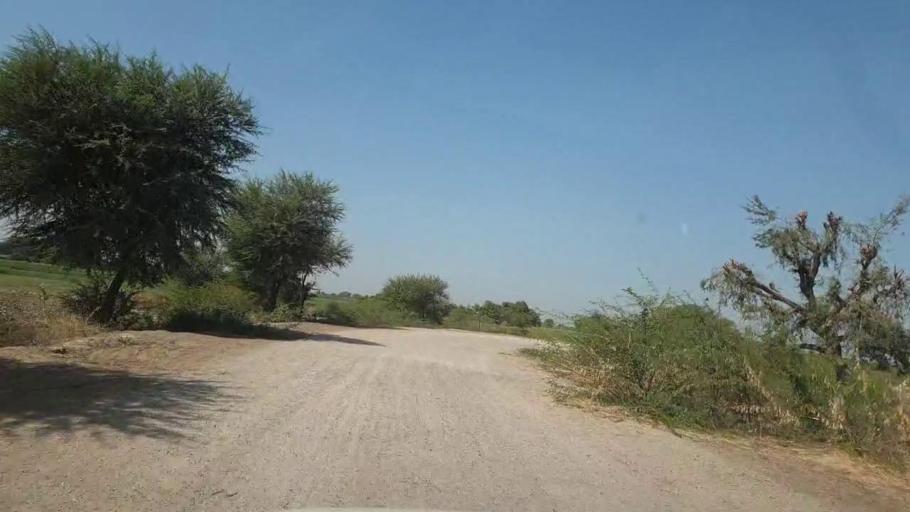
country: PK
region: Sindh
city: Kunri
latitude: 25.1252
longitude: 69.5337
